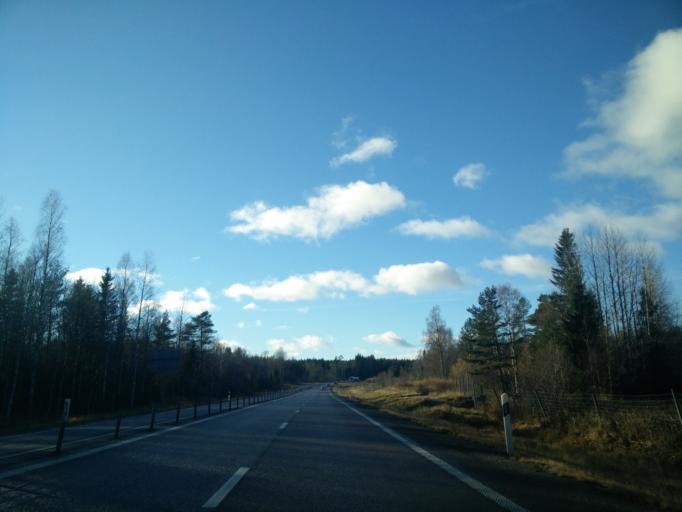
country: SE
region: Vaesternorrland
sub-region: Timra Kommun
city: Soraker
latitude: 62.5363
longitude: 17.5464
